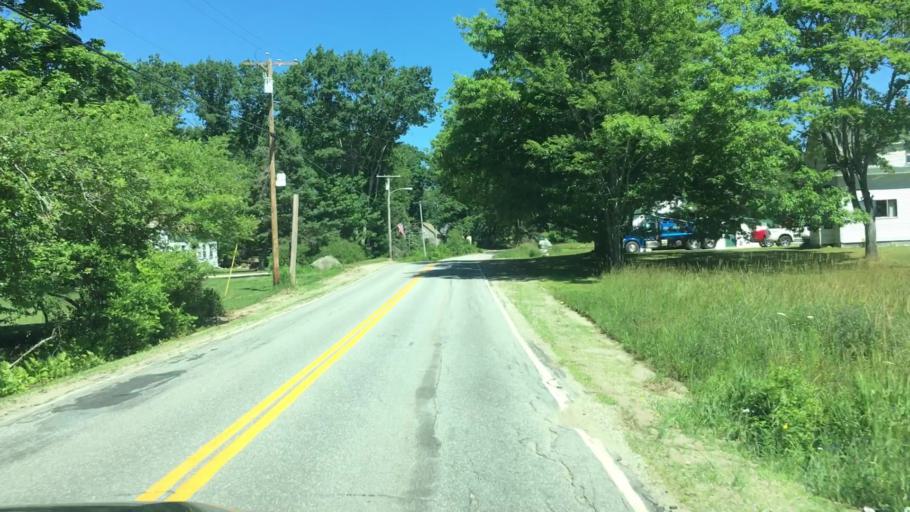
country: US
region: Maine
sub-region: Hancock County
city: Penobscot
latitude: 44.4570
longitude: -68.7042
